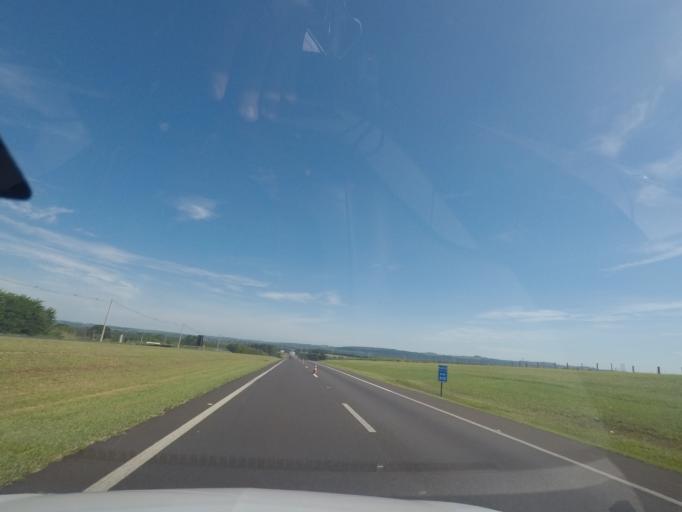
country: BR
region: Sao Paulo
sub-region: Itirapina
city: Itirapina
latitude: -22.1869
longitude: -47.7793
